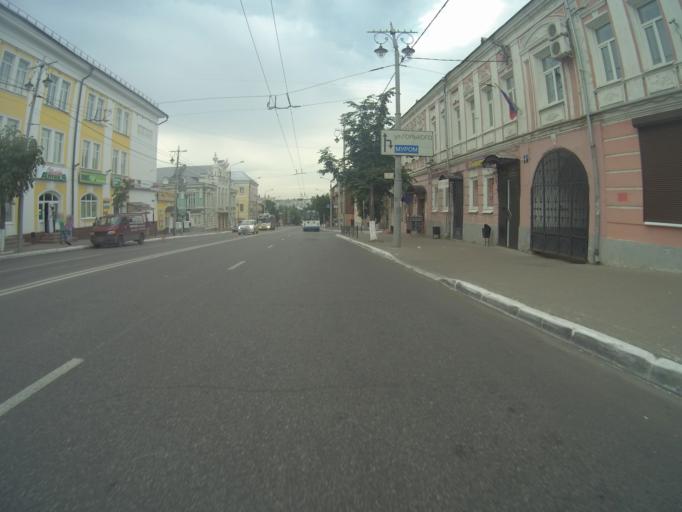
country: RU
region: Vladimir
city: Vladimir
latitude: 56.1293
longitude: 40.4042
